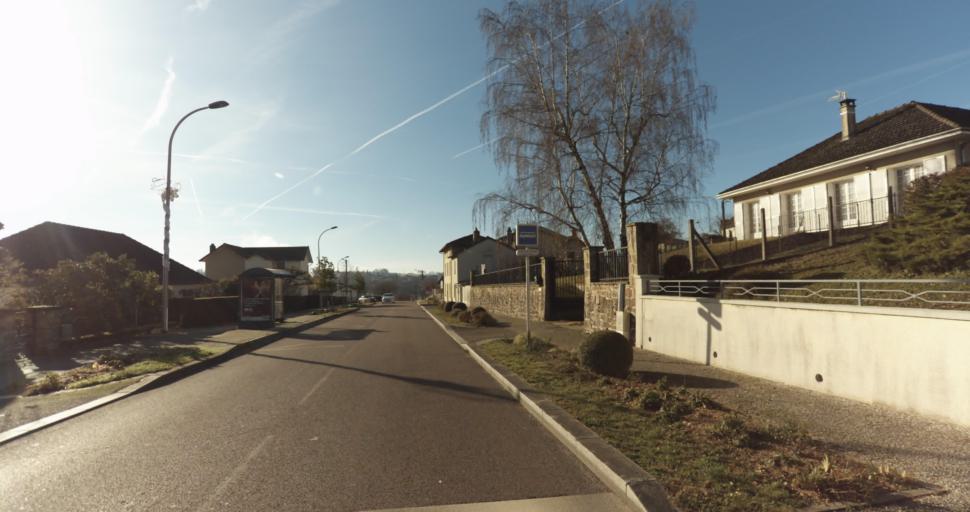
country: FR
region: Limousin
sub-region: Departement de la Haute-Vienne
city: Aixe-sur-Vienne
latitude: 45.7993
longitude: 1.1486
